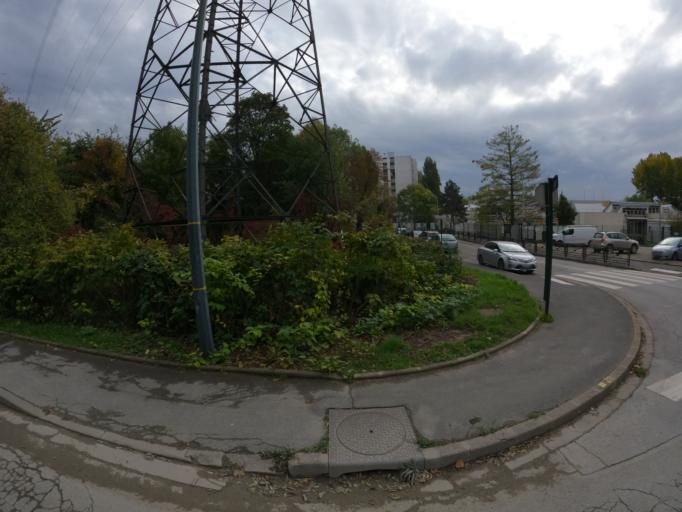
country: FR
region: Ile-de-France
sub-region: Departement de Seine-Saint-Denis
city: Montfermeil
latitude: 48.8857
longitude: 2.5795
